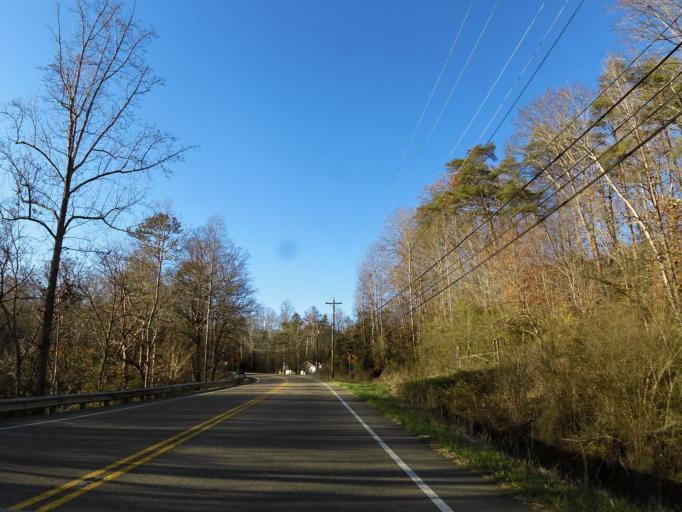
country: US
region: Tennessee
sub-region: Anderson County
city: Clinton
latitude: 36.0653
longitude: -84.2048
